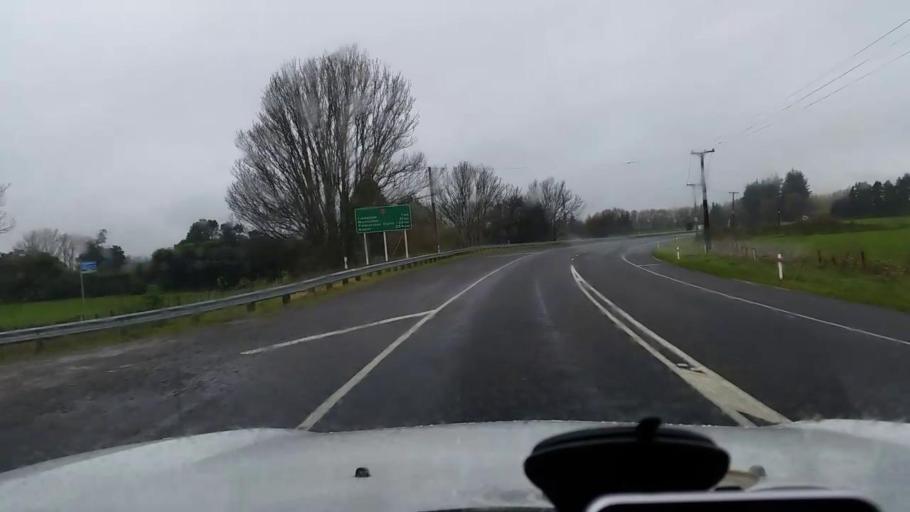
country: NZ
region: Wellington
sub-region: Masterton District
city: Masterton
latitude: -41.0685
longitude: 175.4736
